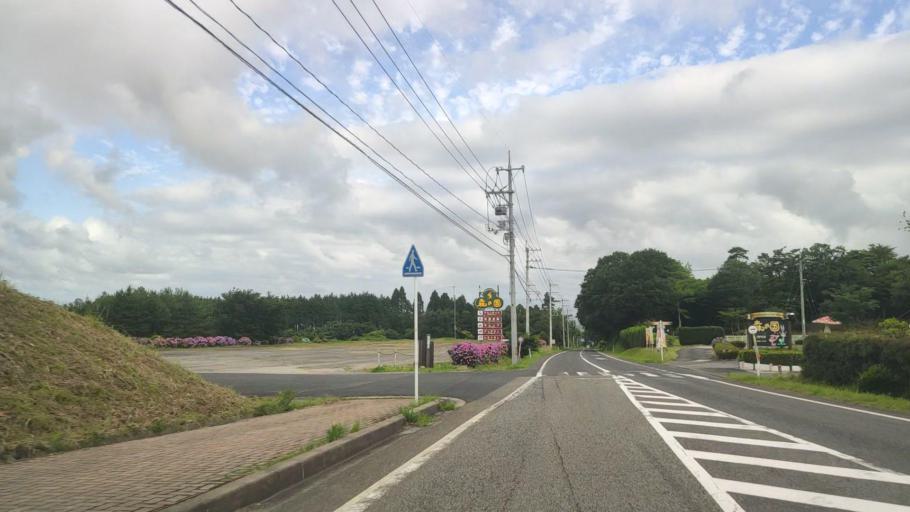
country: JP
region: Tottori
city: Yonago
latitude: 35.4100
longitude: 133.4758
